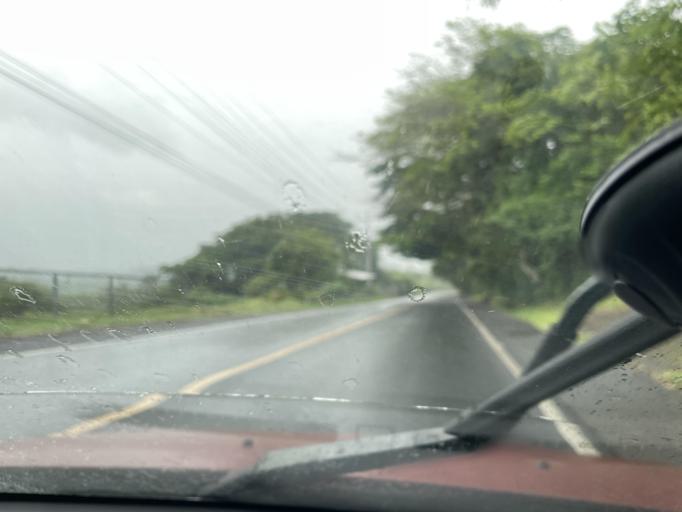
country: SV
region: San Miguel
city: San Miguel
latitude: 13.5316
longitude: -88.1398
